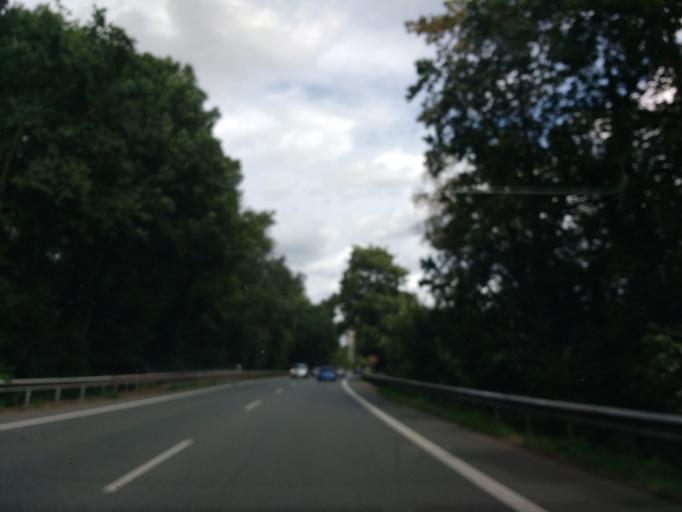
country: DE
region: North Rhine-Westphalia
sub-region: Regierungsbezirk Detmold
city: Petershagen
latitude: 52.3729
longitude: 8.9884
